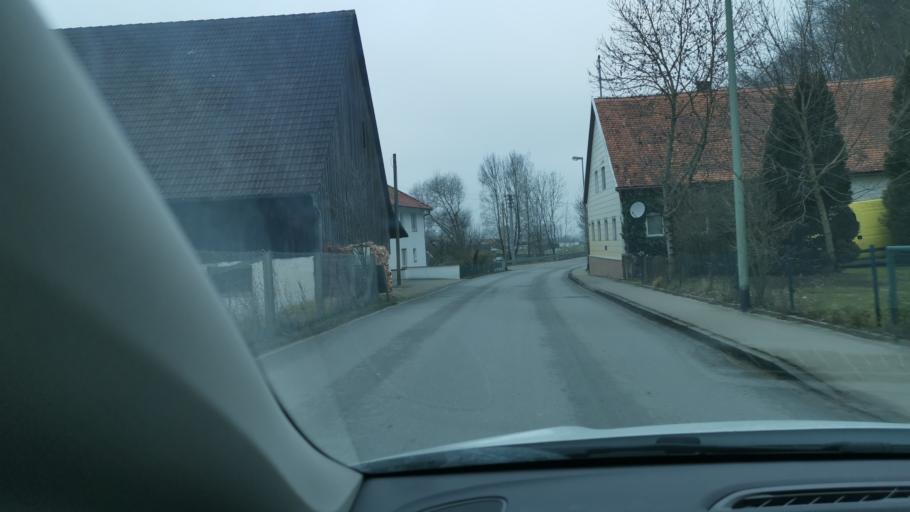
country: DE
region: Bavaria
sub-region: Swabia
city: Rehling
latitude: 48.4877
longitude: 10.9236
